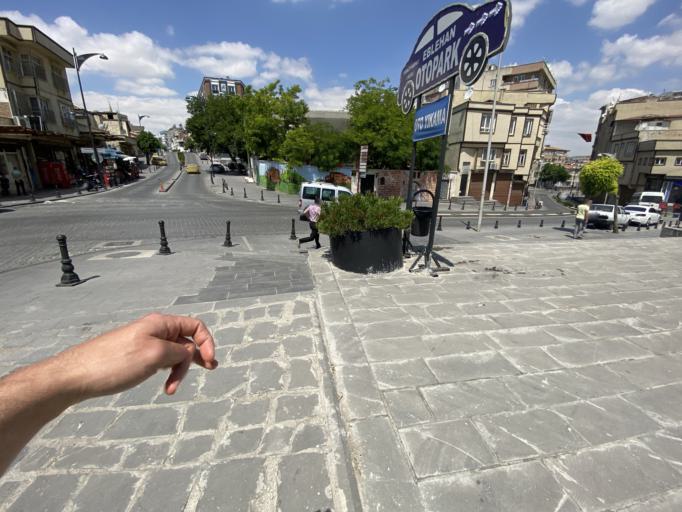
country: TR
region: Gaziantep
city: Gaziantep
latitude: 37.0614
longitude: 37.3759
